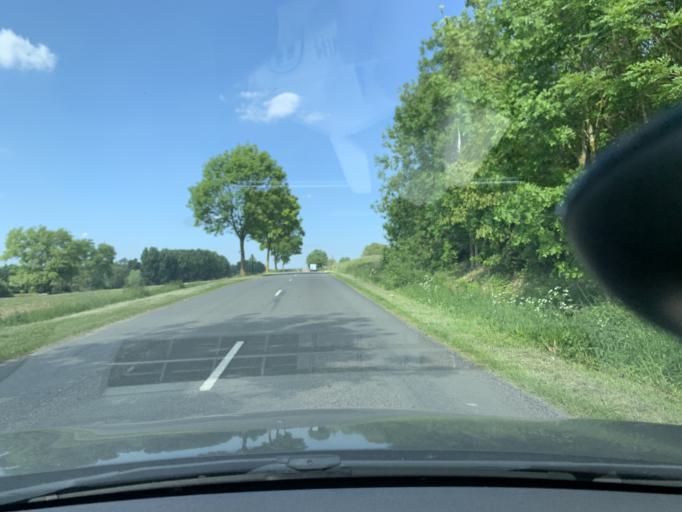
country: FR
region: Nord-Pas-de-Calais
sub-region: Departement du Pas-de-Calais
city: Oisy-le-Verger
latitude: 50.2363
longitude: 3.1088
